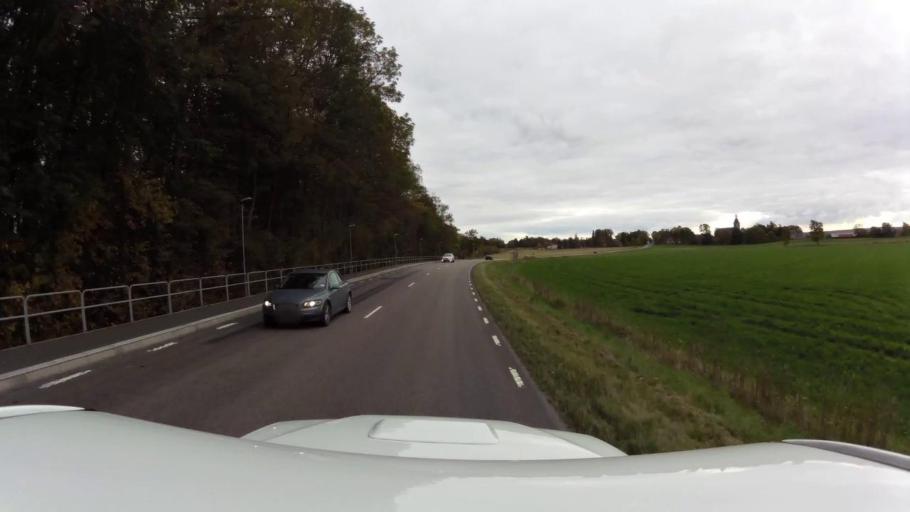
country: SE
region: OEstergoetland
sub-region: Linkopings Kommun
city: Berg
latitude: 58.4874
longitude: 15.5117
